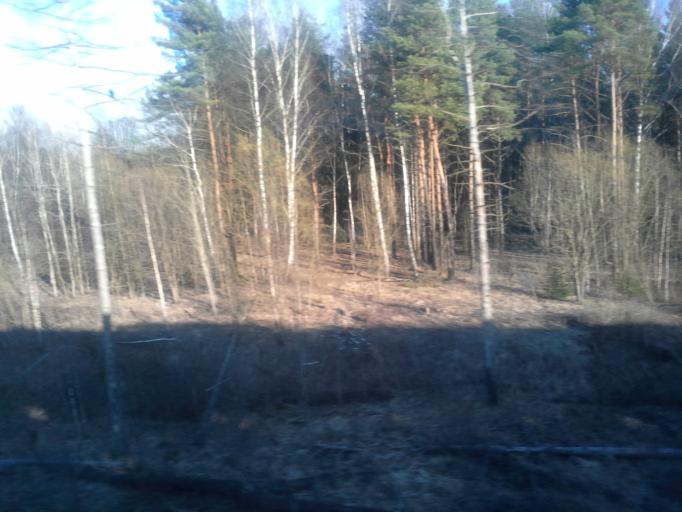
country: RU
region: Moskovskaya
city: Nekrasovskiy
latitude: 56.1035
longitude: 37.5120
